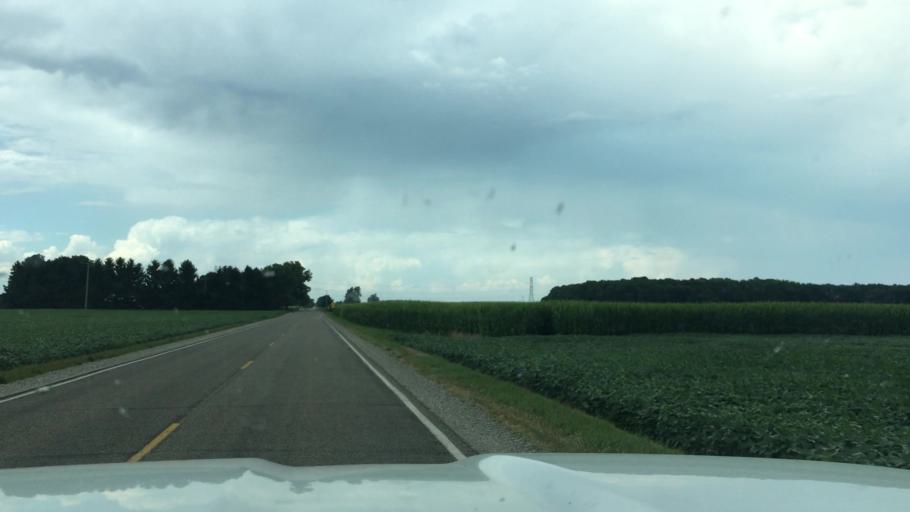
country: US
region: Michigan
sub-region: Montcalm County
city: Carson City
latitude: 43.2014
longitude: -84.7779
